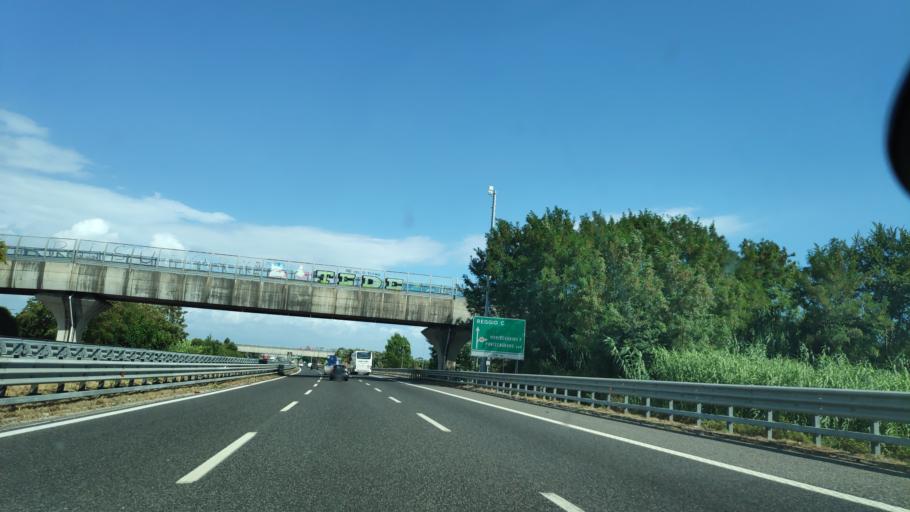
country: IT
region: Campania
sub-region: Provincia di Salerno
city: Sant'Antonio
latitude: 40.6377
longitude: 14.9065
